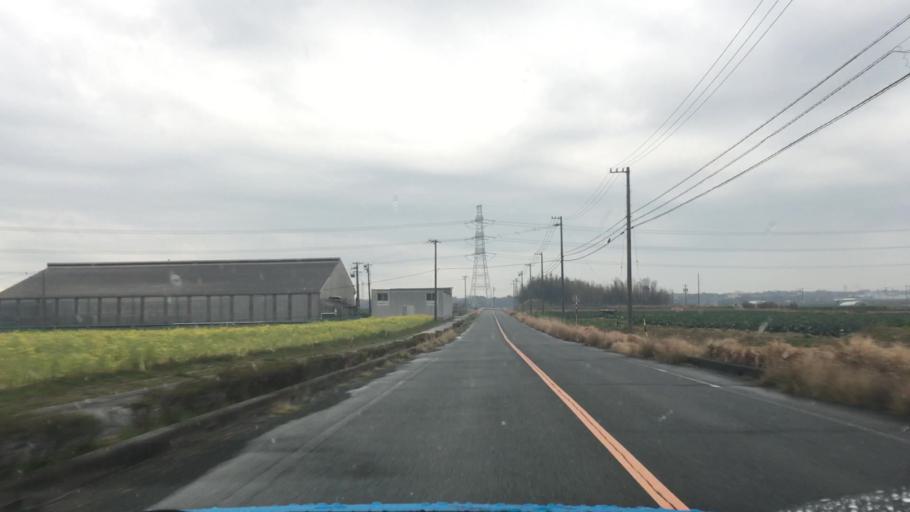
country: JP
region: Aichi
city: Toyohashi
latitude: 34.6785
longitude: 137.3901
